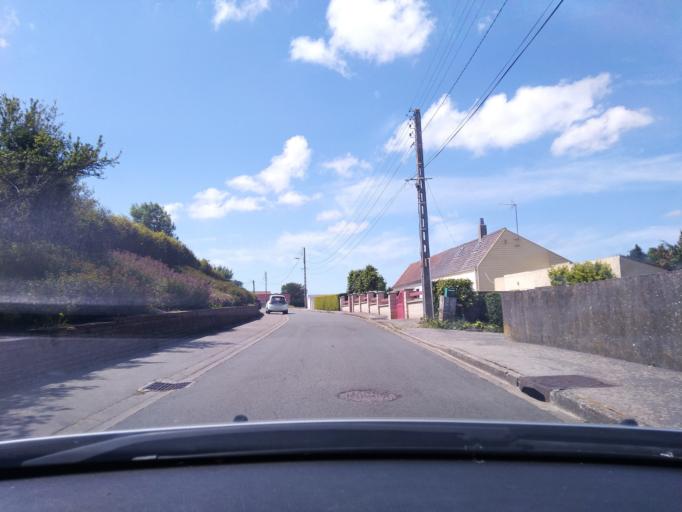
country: FR
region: Nord-Pas-de-Calais
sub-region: Departement du Pas-de-Calais
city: Ferques
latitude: 50.8383
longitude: 1.7575
